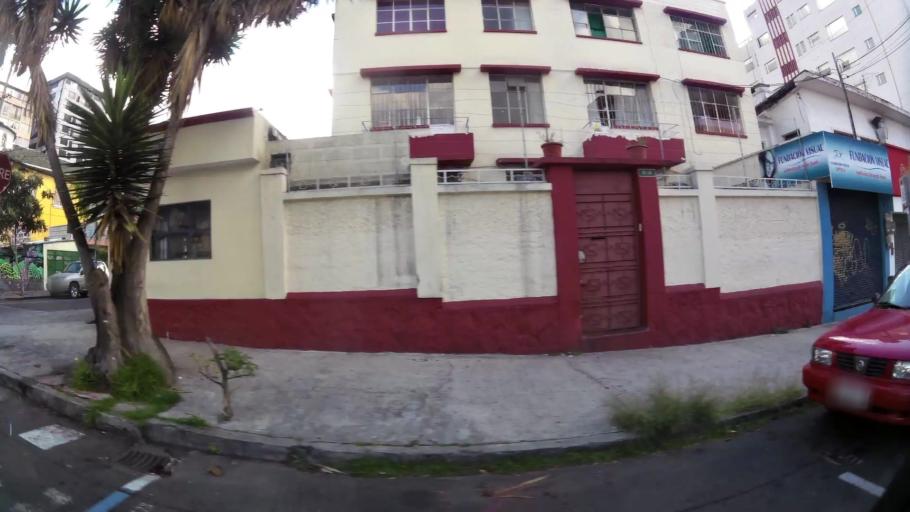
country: EC
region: Pichincha
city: Quito
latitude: -0.2075
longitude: -78.4916
